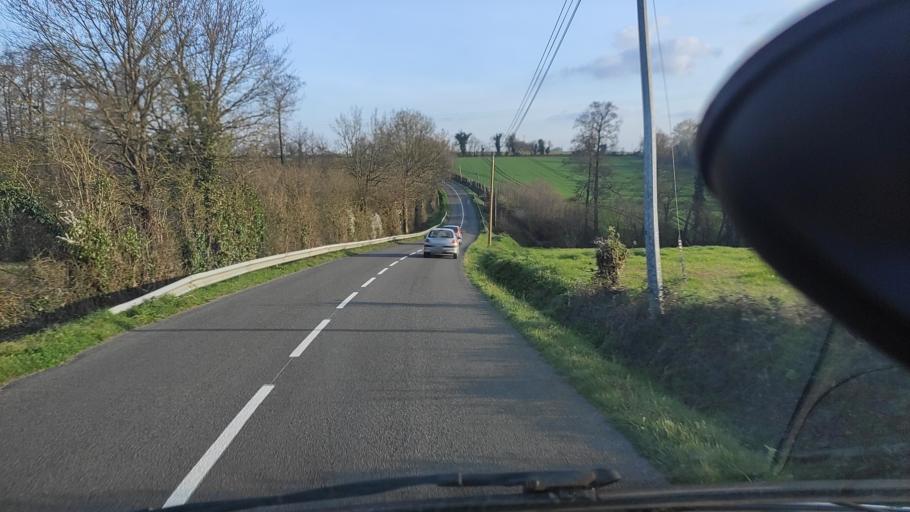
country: FR
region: Pays de la Loire
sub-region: Departement de la Vendee
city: La Chaize-le-Vicomte
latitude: 46.6543
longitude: -1.2982
